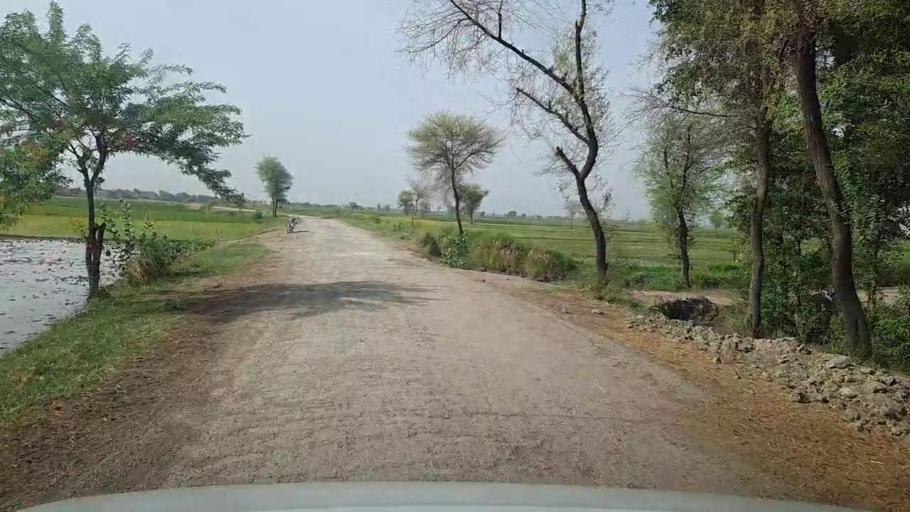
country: PK
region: Sindh
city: Sita Road
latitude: 27.1040
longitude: 67.8214
